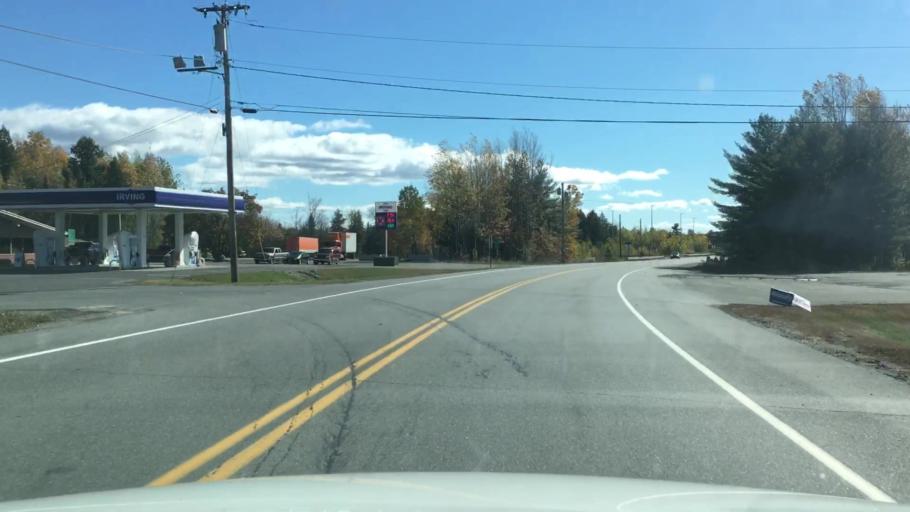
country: US
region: Maine
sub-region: Penobscot County
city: Medway
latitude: 45.6100
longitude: -68.5245
